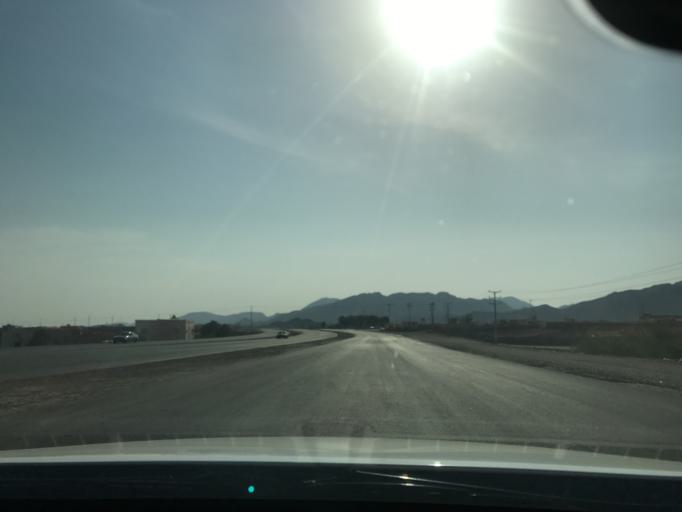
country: SA
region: Makkah
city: Al Jumum
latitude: 21.4538
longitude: 39.5375
